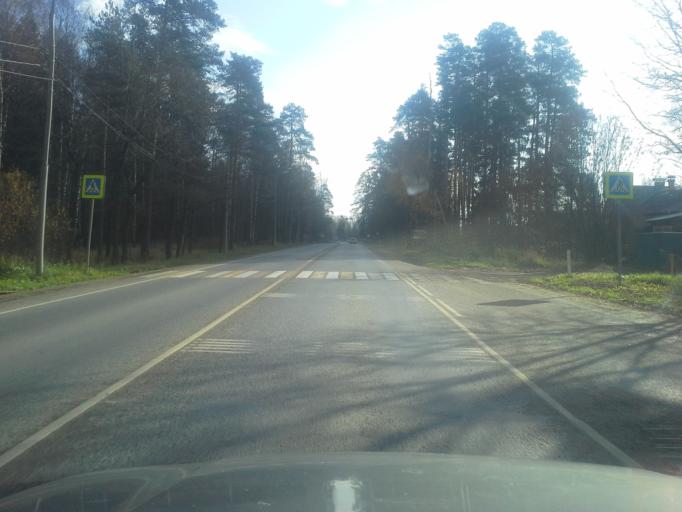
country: RU
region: Moskovskaya
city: Bol'shiye Vyazemy
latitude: 55.6703
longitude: 36.9515
